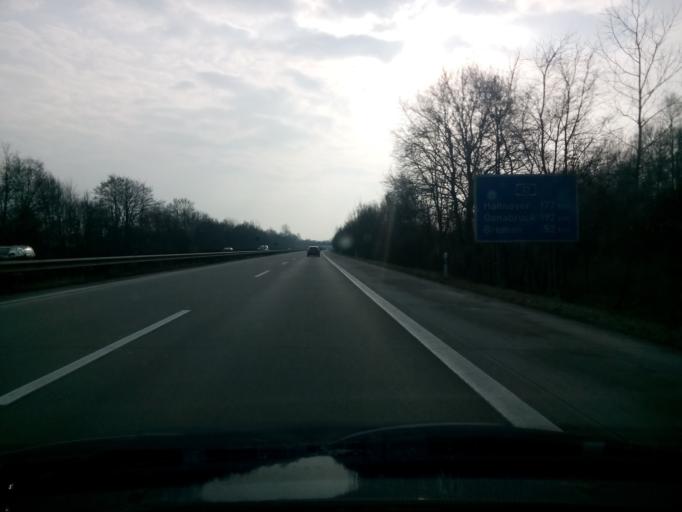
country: DE
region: Lower Saxony
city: Loxstedt
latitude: 53.4887
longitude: 8.6233
